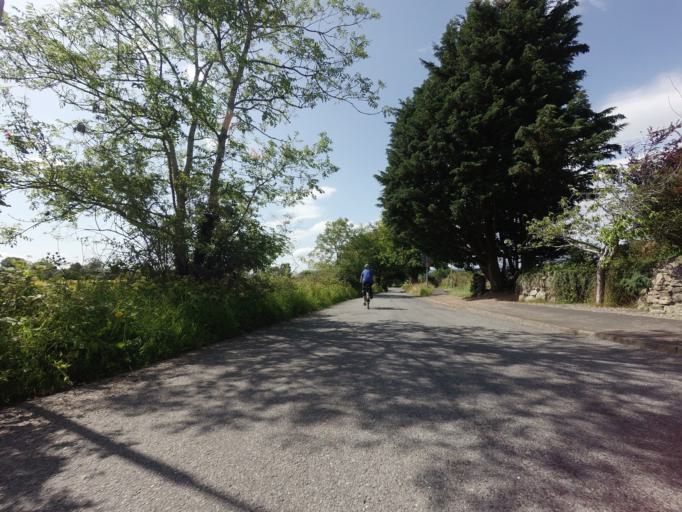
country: GB
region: Scotland
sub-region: Highland
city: Fortrose
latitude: 57.4948
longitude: -4.1236
